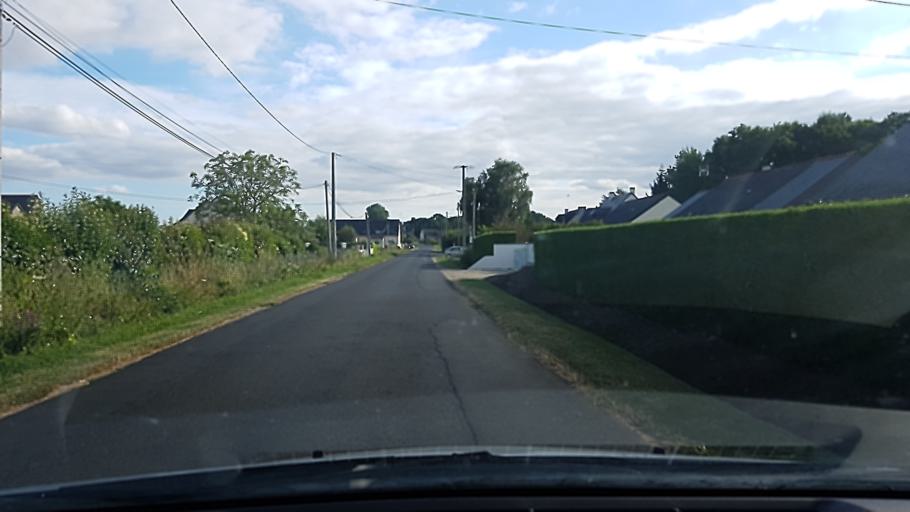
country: FR
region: Pays de la Loire
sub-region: Departement de Maine-et-Loire
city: Maze
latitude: 47.4856
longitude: -0.2770
